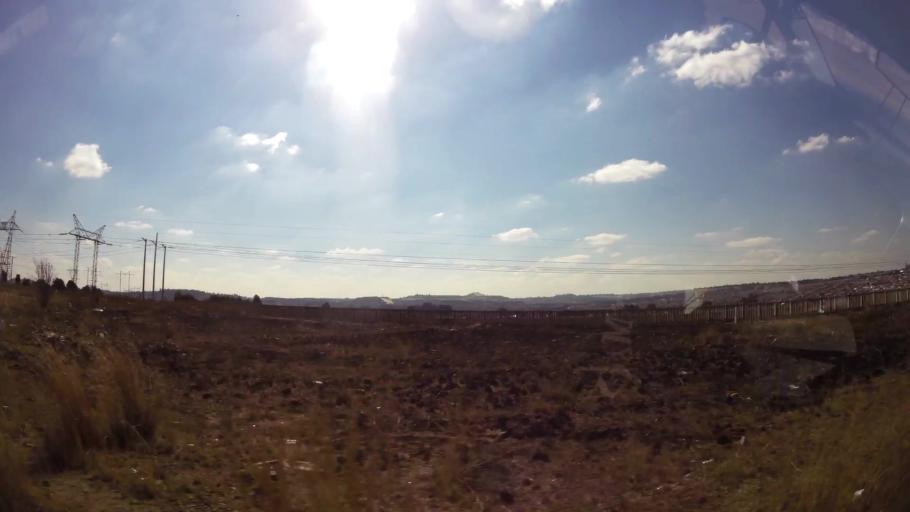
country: ZA
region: Gauteng
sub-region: West Rand District Municipality
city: Randfontein
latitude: -26.1630
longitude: 27.7561
